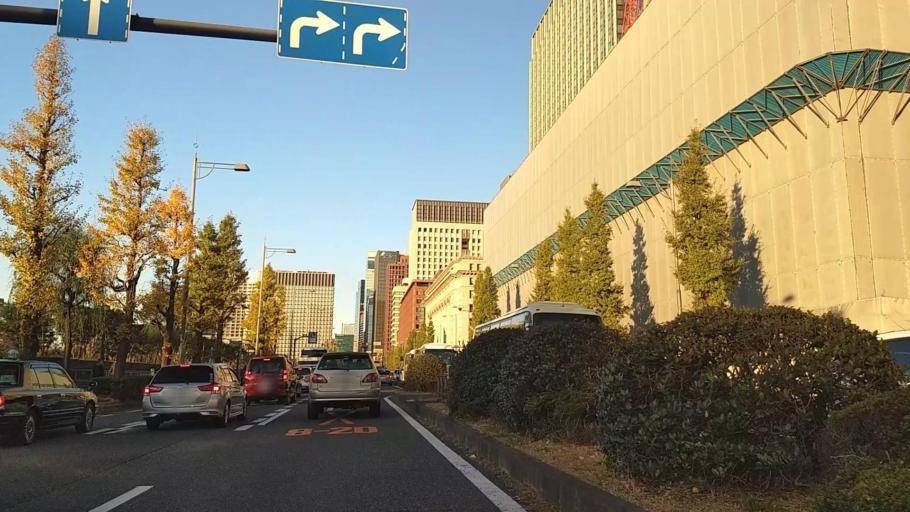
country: JP
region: Tokyo
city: Tokyo
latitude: 35.6772
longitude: 139.7605
